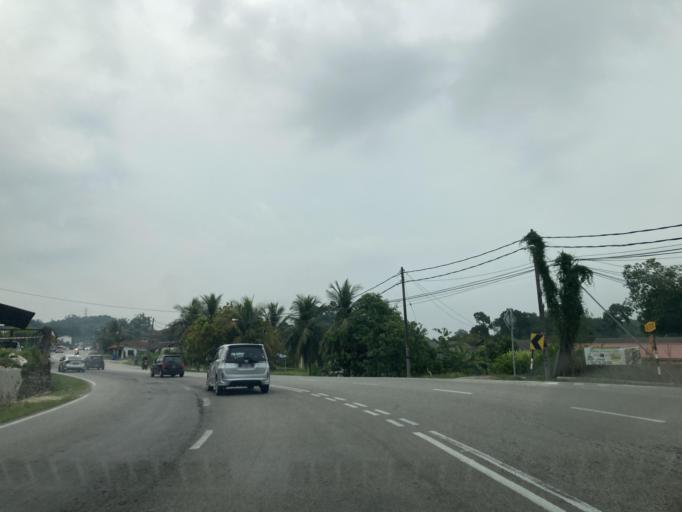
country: MY
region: Selangor
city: Kuang
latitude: 3.2141
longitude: 101.5347
